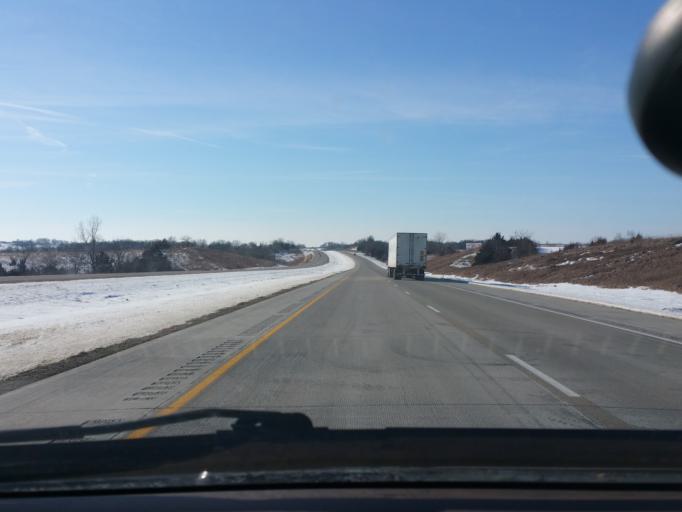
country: US
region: Iowa
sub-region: Decatur County
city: Lamoni
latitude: 40.6381
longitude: -93.8757
